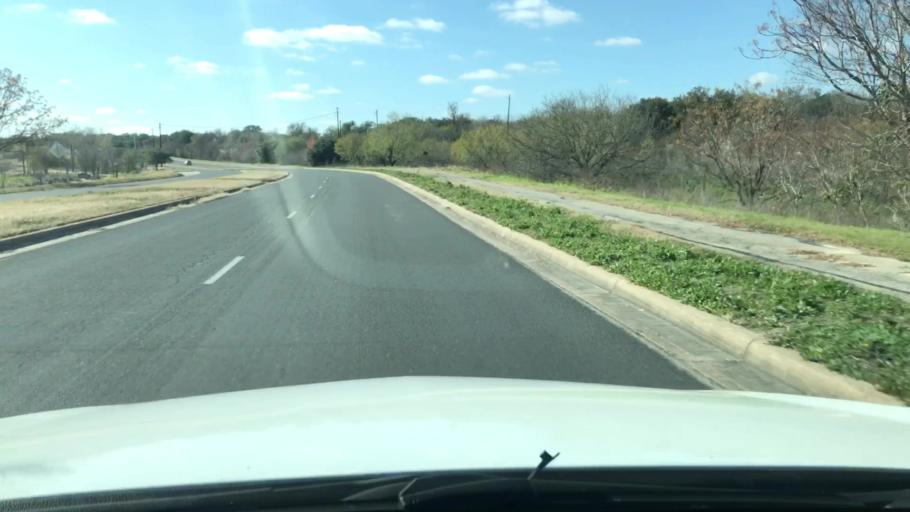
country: US
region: Texas
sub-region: Travis County
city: Onion Creek
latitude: 30.1832
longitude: -97.7189
